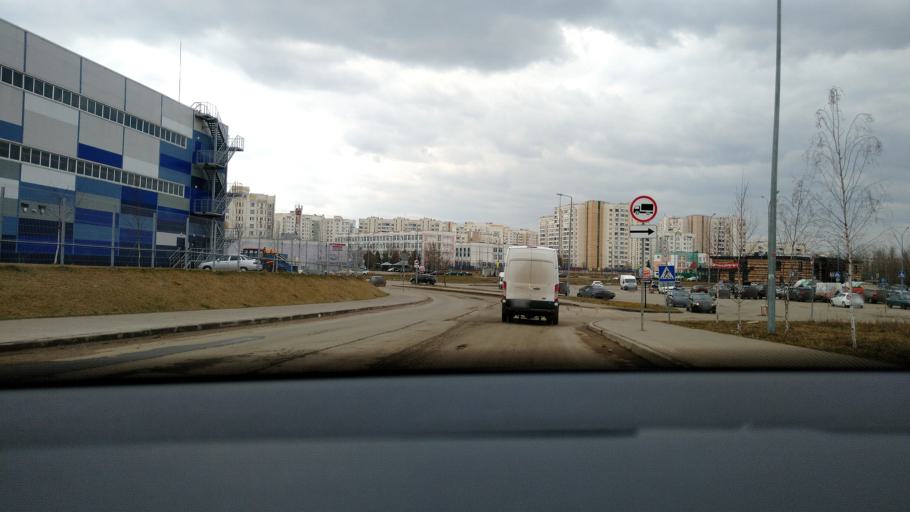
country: RU
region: Moskovskaya
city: Kommunarka
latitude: 55.5523
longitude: 37.5303
